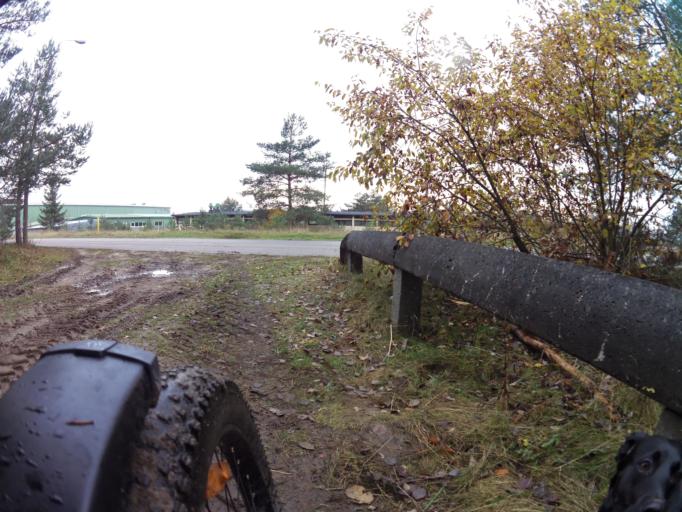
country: PL
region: Pomeranian Voivodeship
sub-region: Powiat pucki
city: Krokowa
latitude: 54.7404
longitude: 18.0983
